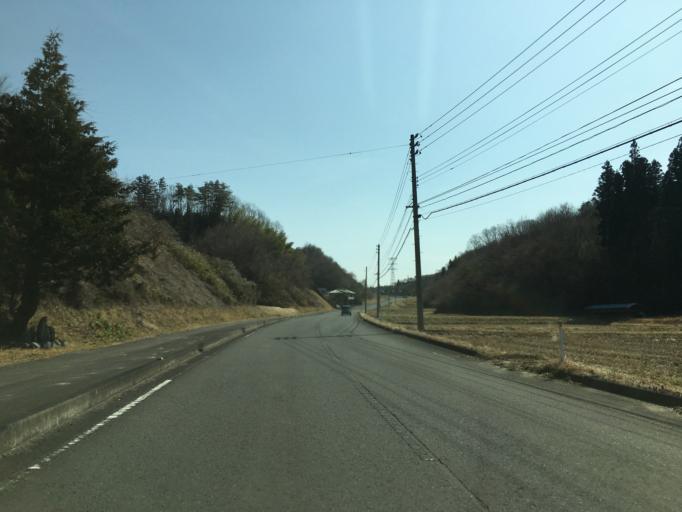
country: JP
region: Fukushima
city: Ishikawa
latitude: 37.0431
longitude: 140.4701
